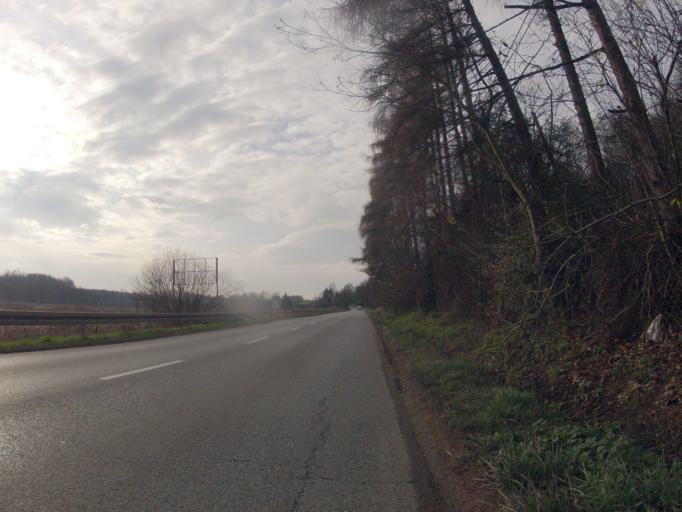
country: PL
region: Lesser Poland Voivodeship
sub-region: Powiat krakowski
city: Rzaska
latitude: 50.0906
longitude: 19.8229
